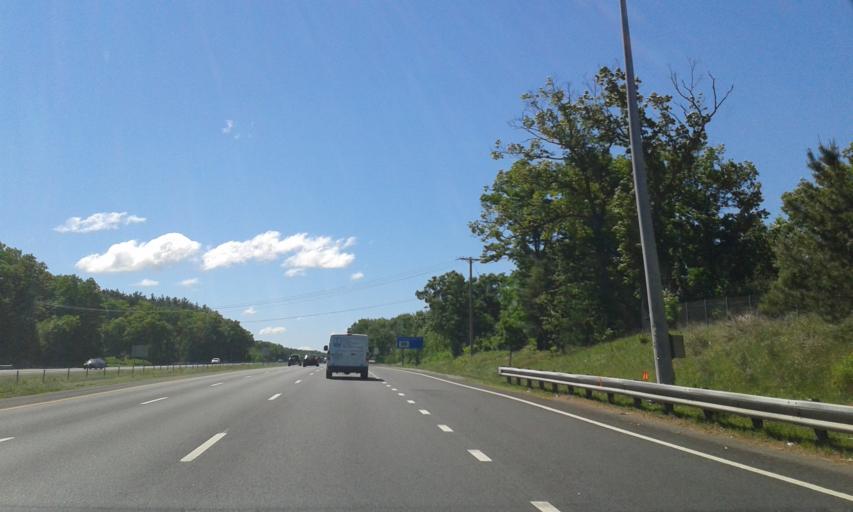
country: US
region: Massachusetts
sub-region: Middlesex County
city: Billerica
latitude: 42.5597
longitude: -71.2972
